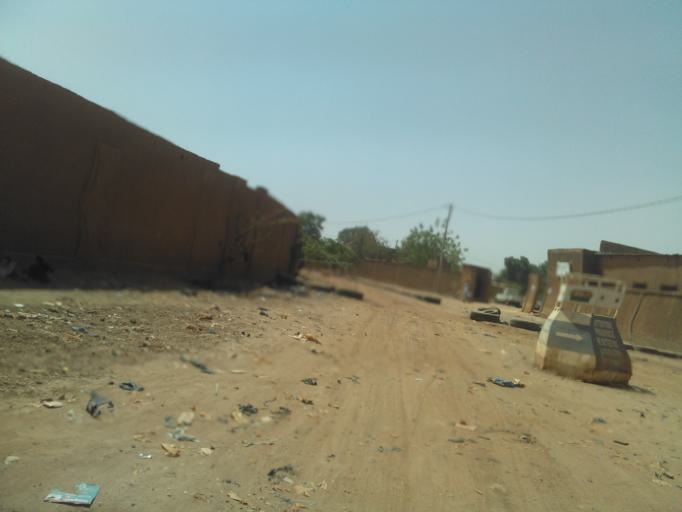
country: BF
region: Centre
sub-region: Kadiogo Province
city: Ouagadougou
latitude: 12.3939
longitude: -1.5724
